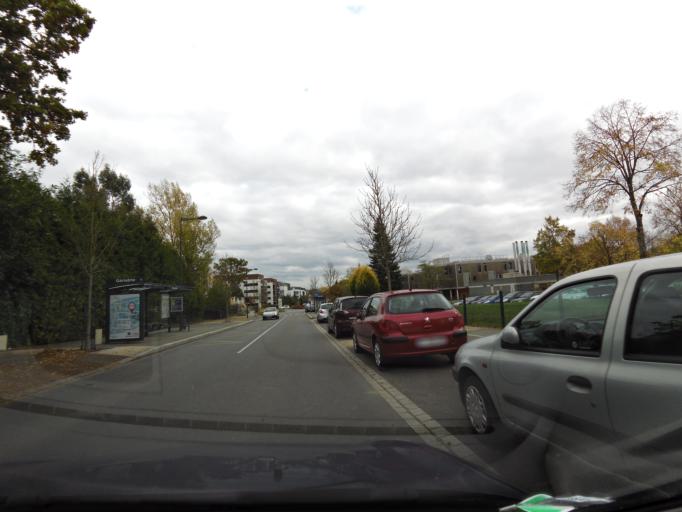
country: FR
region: Brittany
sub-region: Departement d'Ille-et-Vilaine
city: Chantepie
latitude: 48.0852
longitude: -1.6111
